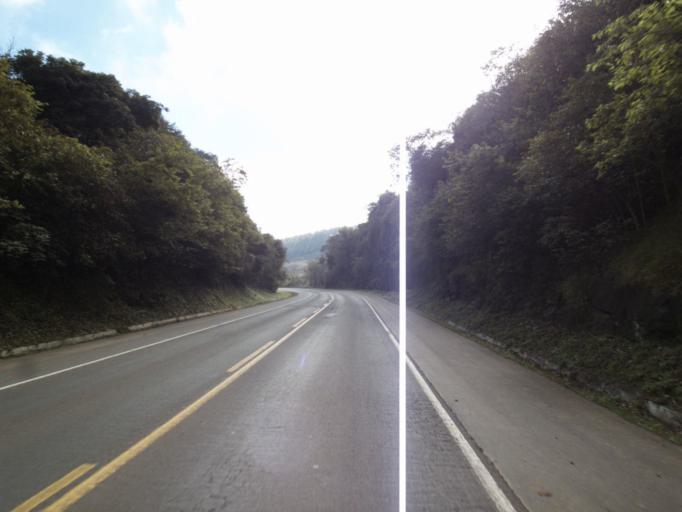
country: BR
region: Rio Grande do Sul
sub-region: Frederico Westphalen
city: Frederico Westphalen
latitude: -27.1466
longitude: -53.2130
